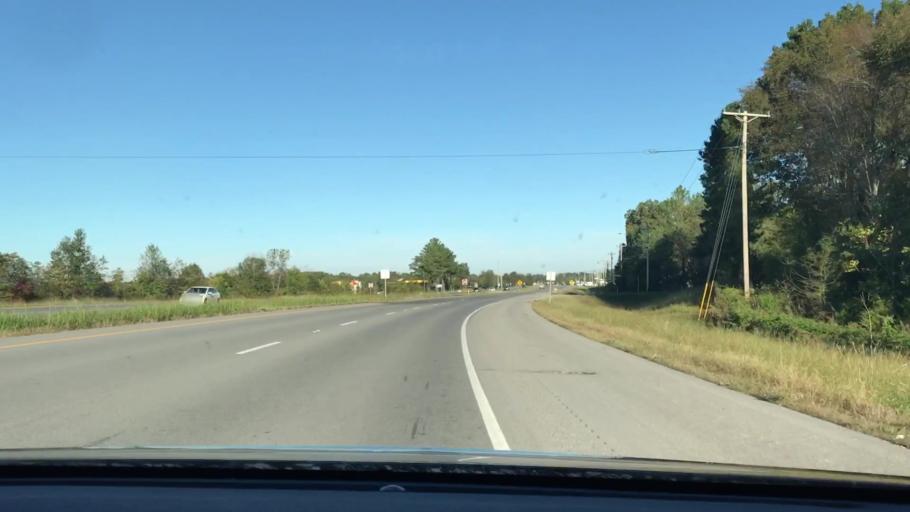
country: US
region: Kentucky
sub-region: Christian County
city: Hopkinsville
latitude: 36.8189
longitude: -87.5005
